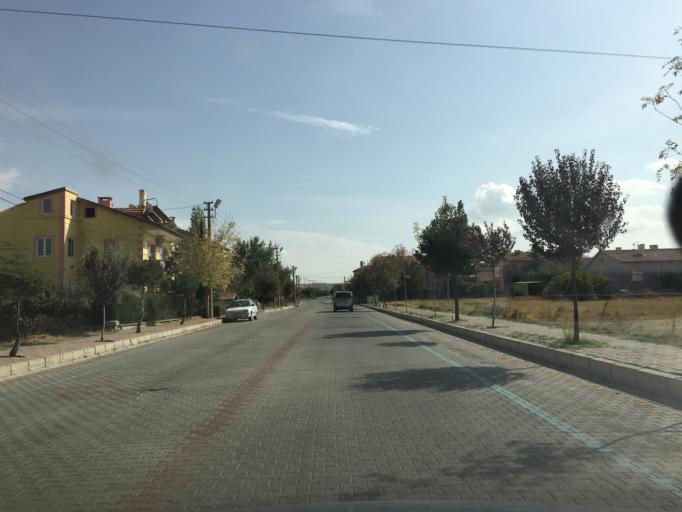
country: TR
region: Nevsehir
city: Avanos
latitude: 38.7068
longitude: 34.8527
